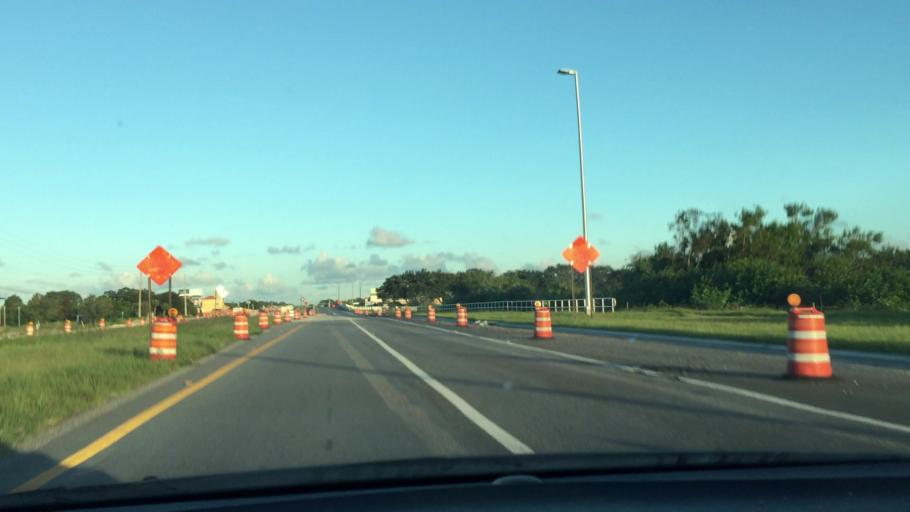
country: US
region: Florida
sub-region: Osceola County
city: Saint Cloud
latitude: 28.2594
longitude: -81.3255
